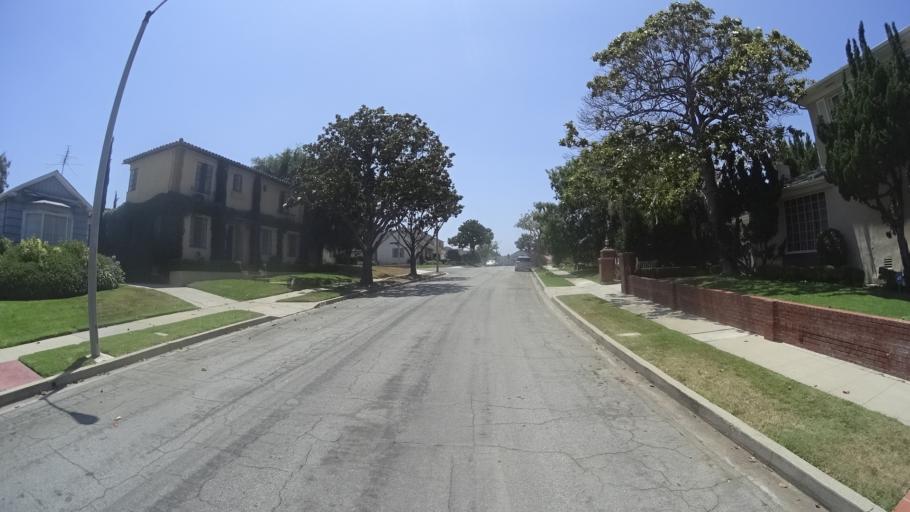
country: US
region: California
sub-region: Los Angeles County
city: View Park-Windsor Hills
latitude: 34.0004
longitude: -118.3444
